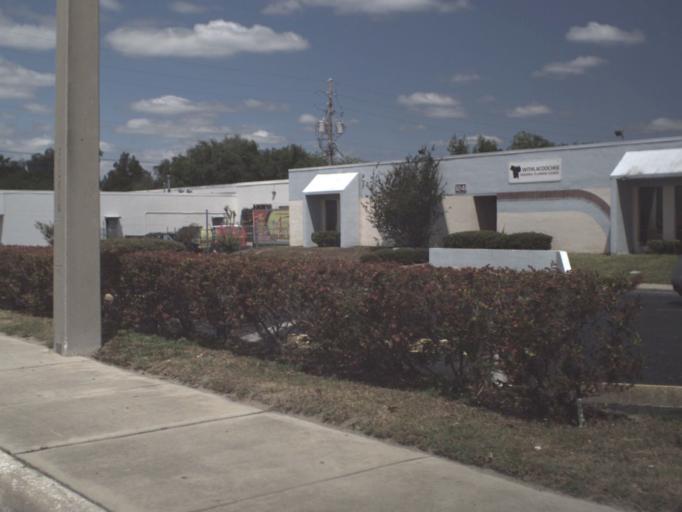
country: US
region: Florida
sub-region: Marion County
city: Ocala
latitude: 29.1791
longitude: -82.1507
